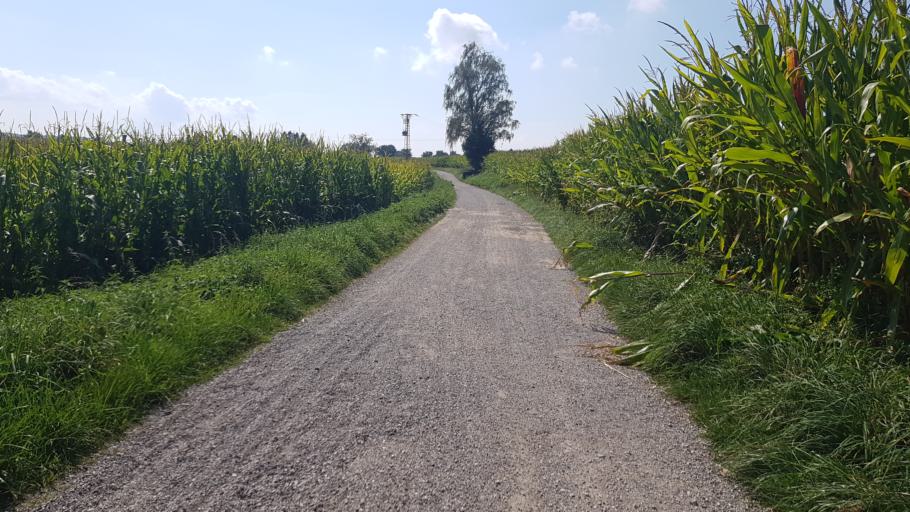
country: DE
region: Bavaria
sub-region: Upper Bavaria
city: Worthsee
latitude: 48.0462
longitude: 11.1939
